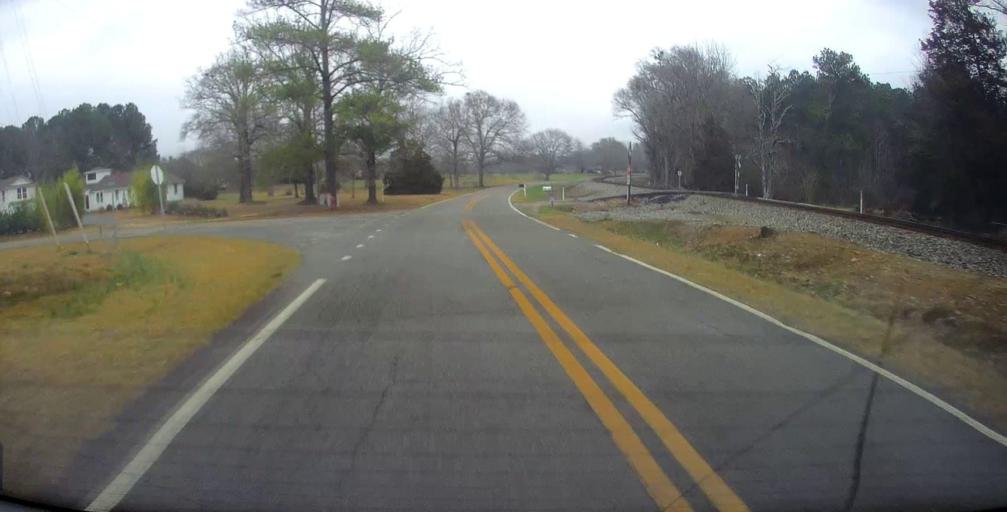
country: US
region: Georgia
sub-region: Lamar County
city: Barnesville
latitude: 33.0761
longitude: -84.1002
